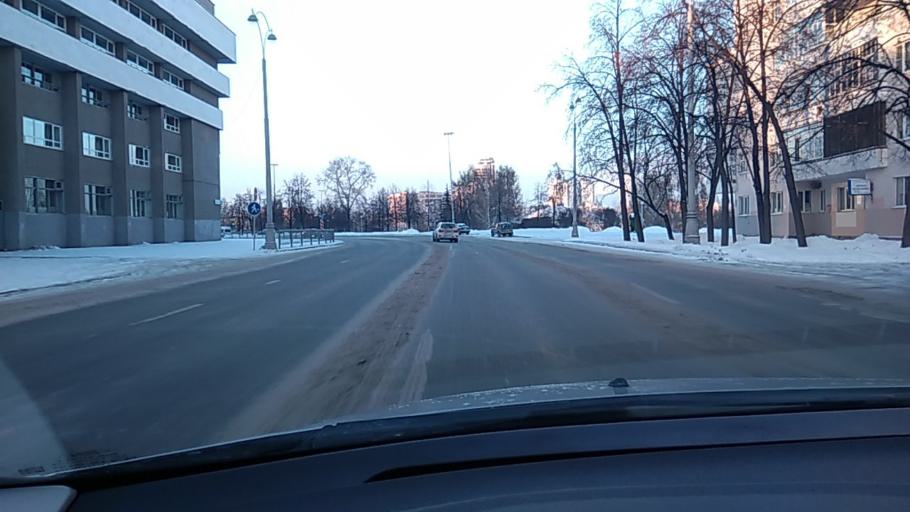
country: RU
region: Sverdlovsk
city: Yekaterinburg
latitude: 56.8405
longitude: 60.5979
